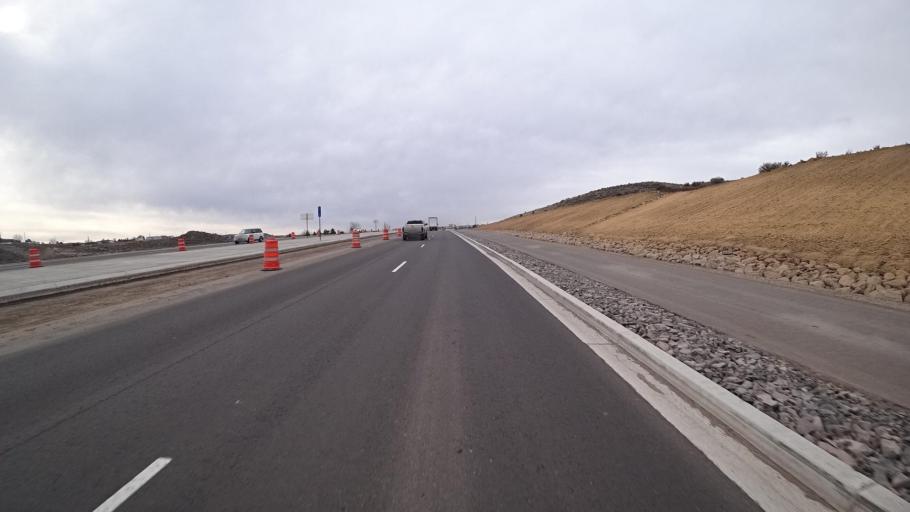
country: US
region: Nevada
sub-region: Washoe County
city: Lemmon Valley
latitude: 39.6201
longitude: -119.8489
